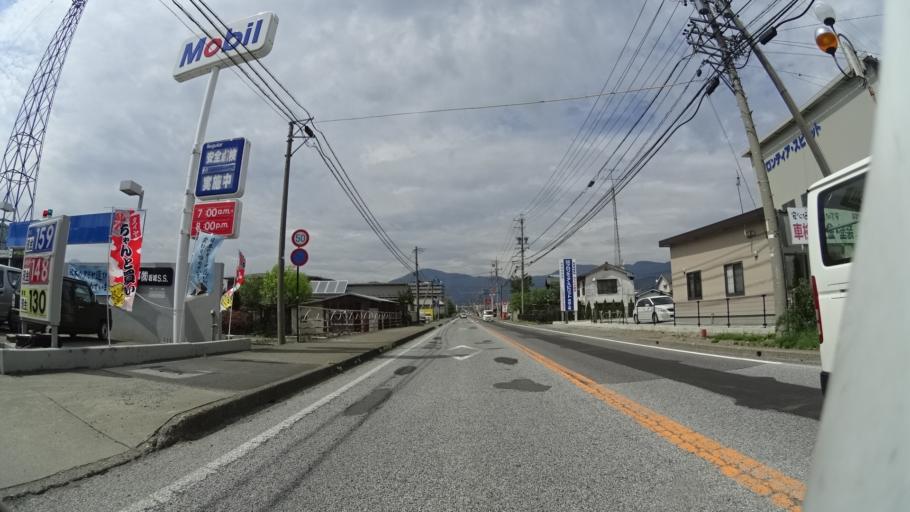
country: JP
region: Nagano
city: Ueda
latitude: 36.4319
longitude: 138.1925
